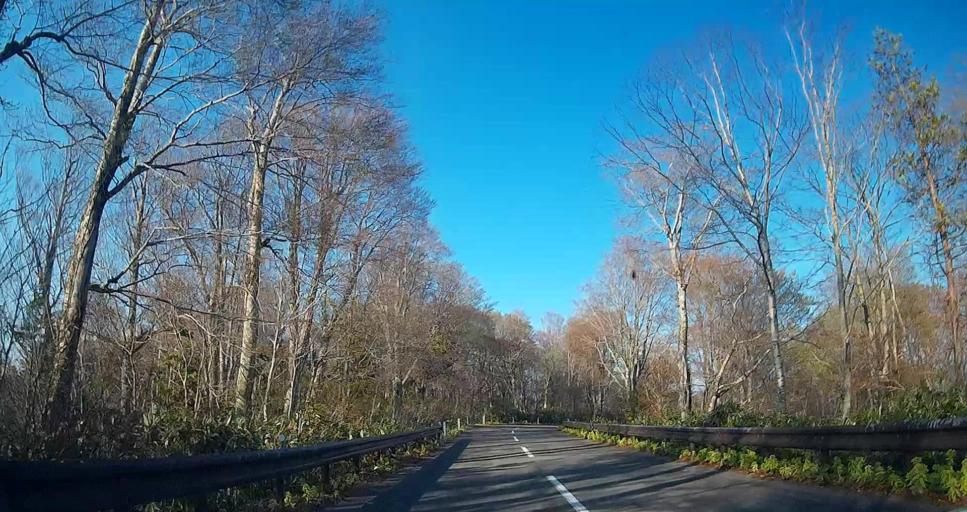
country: JP
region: Aomori
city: Mutsu
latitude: 41.3072
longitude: 141.1170
